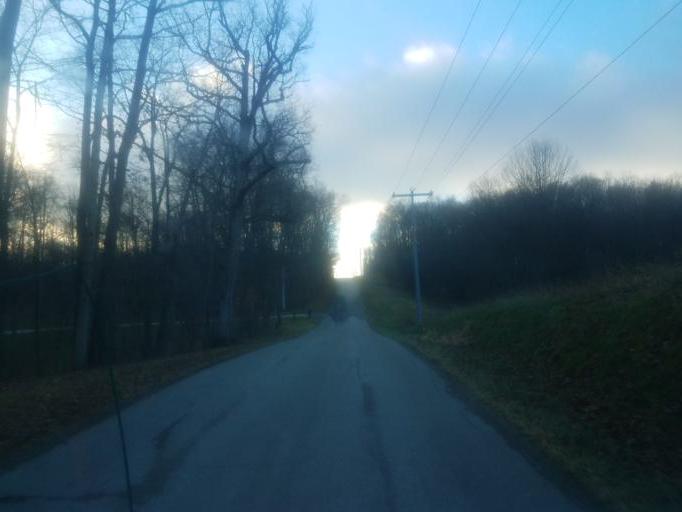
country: US
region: Ohio
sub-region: Sandusky County
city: Bellville
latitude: 40.5657
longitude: -82.4976
